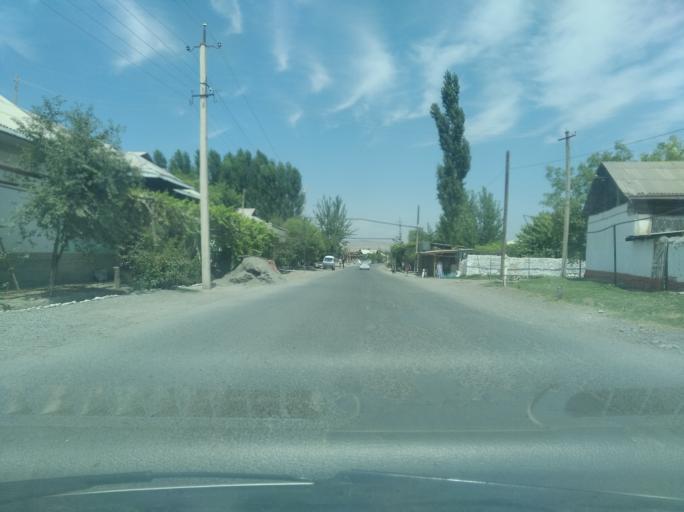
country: KG
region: Osh
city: Aravan
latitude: 40.6174
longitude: 72.4541
